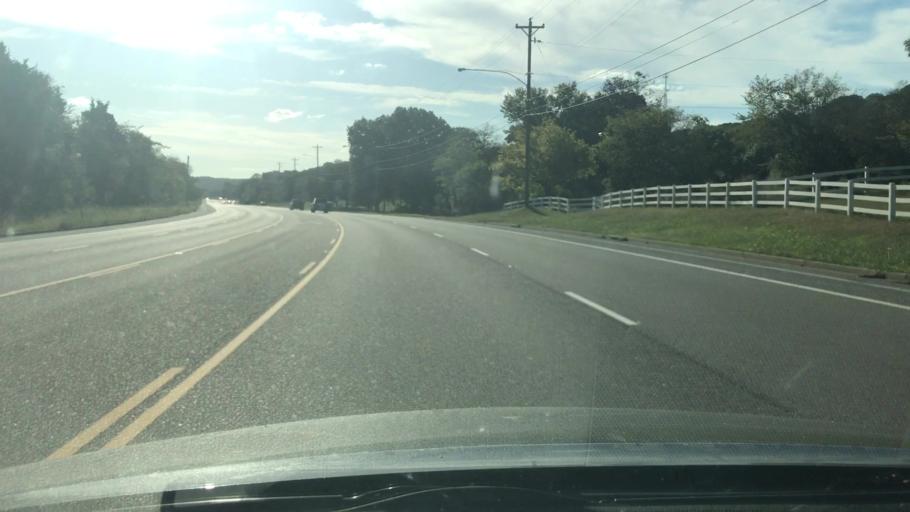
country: US
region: Tennessee
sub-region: Davidson County
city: Belle Meade
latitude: 36.2113
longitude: -86.9251
